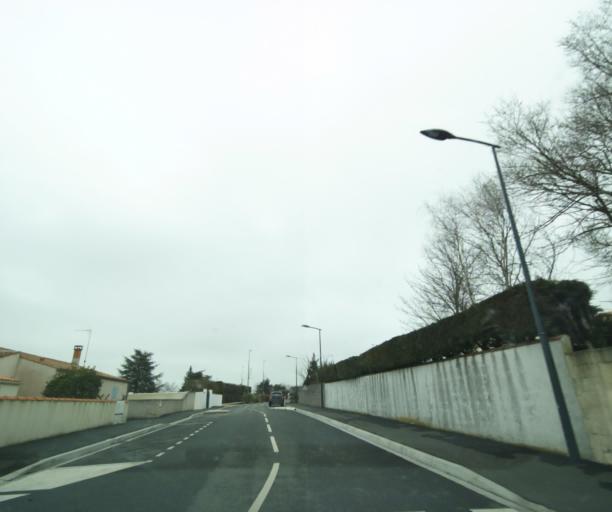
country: FR
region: Poitou-Charentes
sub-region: Departement de la Charente-Maritime
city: Lagord
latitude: 46.1841
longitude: -1.1439
